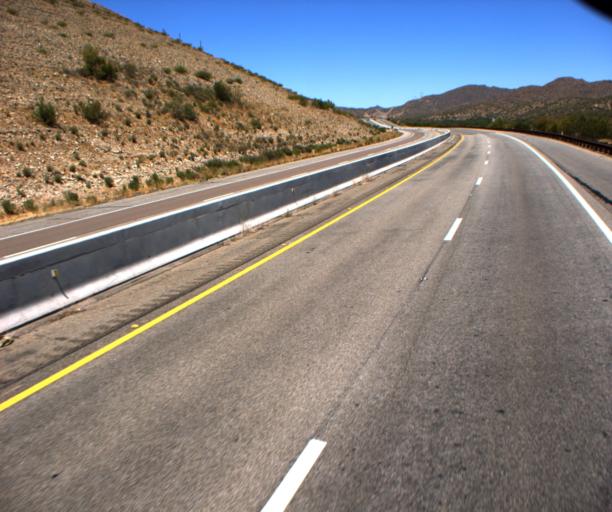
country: US
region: Arizona
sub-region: Yavapai County
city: Bagdad
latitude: 34.3784
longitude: -113.1922
